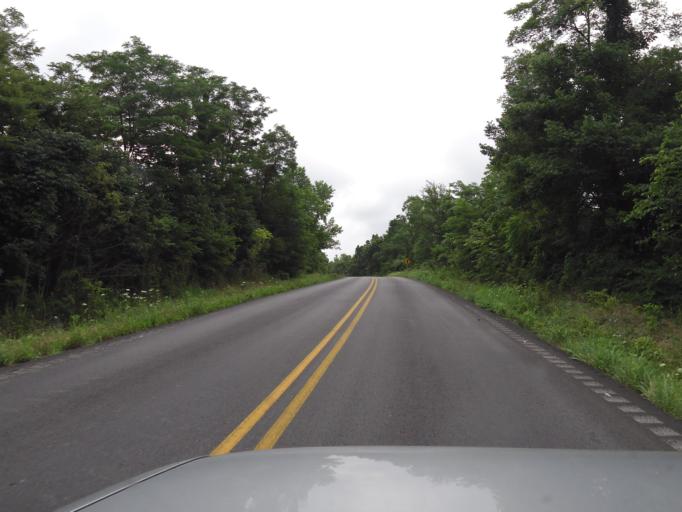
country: US
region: Kentucky
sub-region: Hopkins County
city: Madisonville
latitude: 37.2996
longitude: -87.3621
